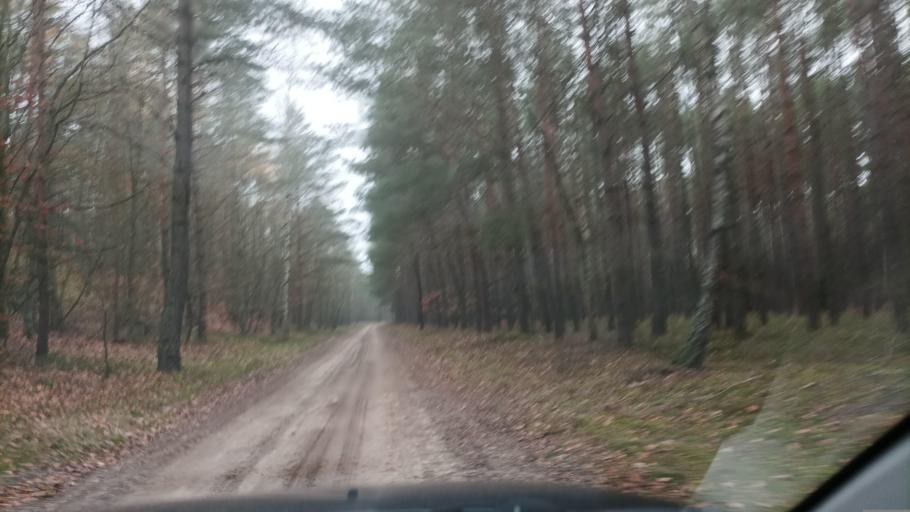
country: PL
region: Greater Poland Voivodeship
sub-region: Powiat czarnkowsko-trzcianecki
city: Polajewo
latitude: 52.7505
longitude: 16.7785
